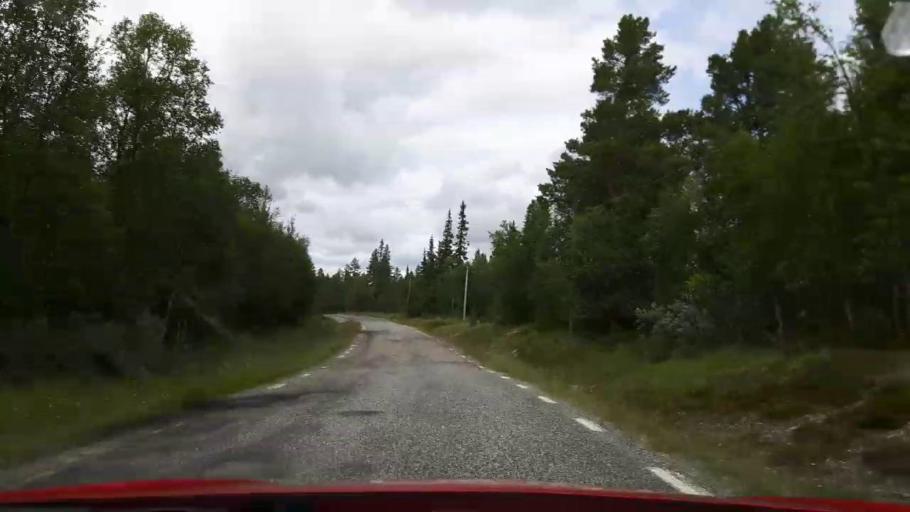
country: NO
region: Hedmark
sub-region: Engerdal
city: Engerdal
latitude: 62.3115
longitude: 12.8102
